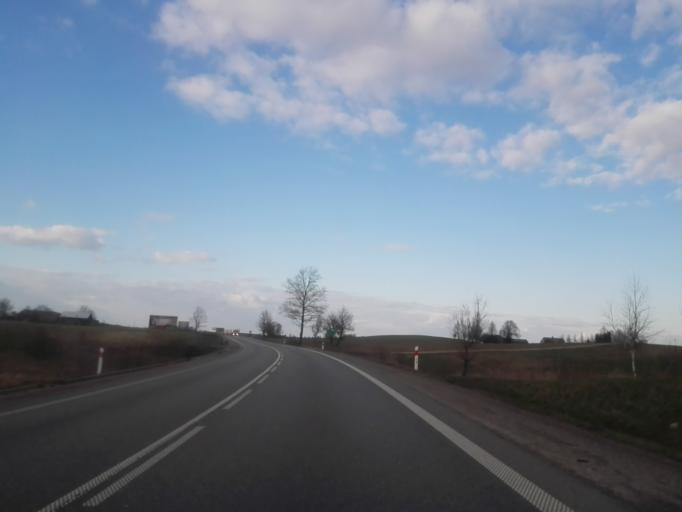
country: PL
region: Podlasie
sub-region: Suwalki
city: Suwalki
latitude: 54.1983
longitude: 23.0194
